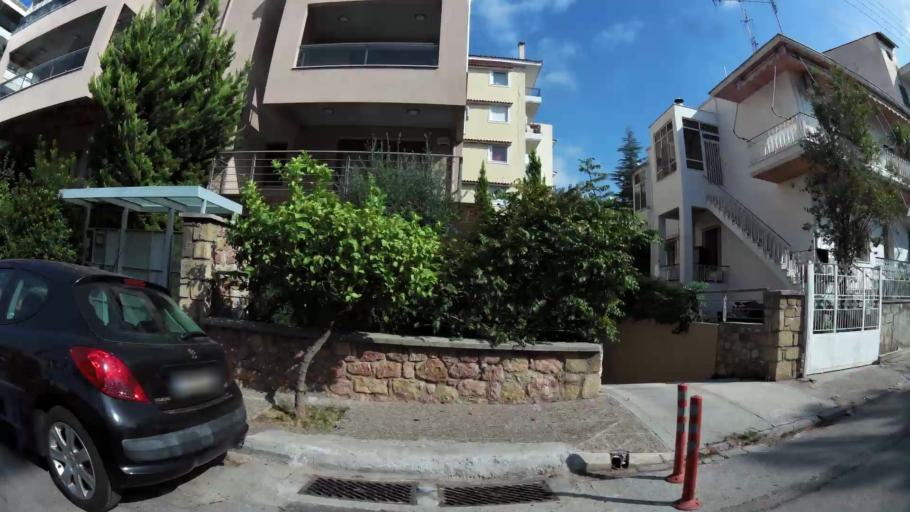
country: GR
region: Attica
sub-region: Nomarchia Athinas
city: Neo Psychiko
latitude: 37.9994
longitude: 23.7883
